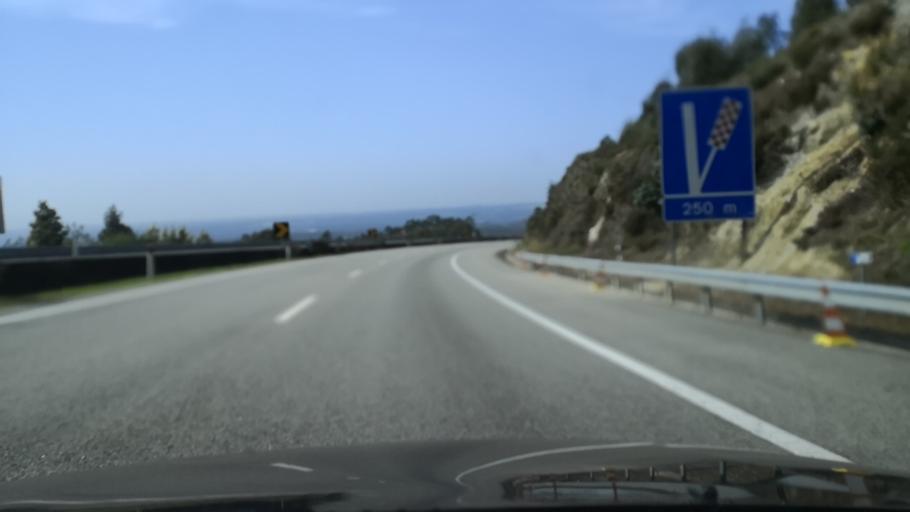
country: PT
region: Aveiro
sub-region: Agueda
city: Valongo
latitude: 40.6503
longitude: -8.3727
